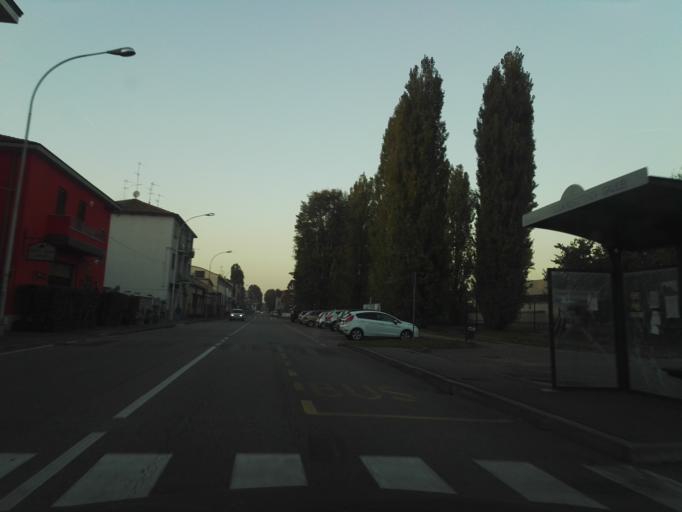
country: IT
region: Lombardy
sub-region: Citta metropolitana di Milano
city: Mezzate
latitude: 45.4385
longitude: 9.2952
